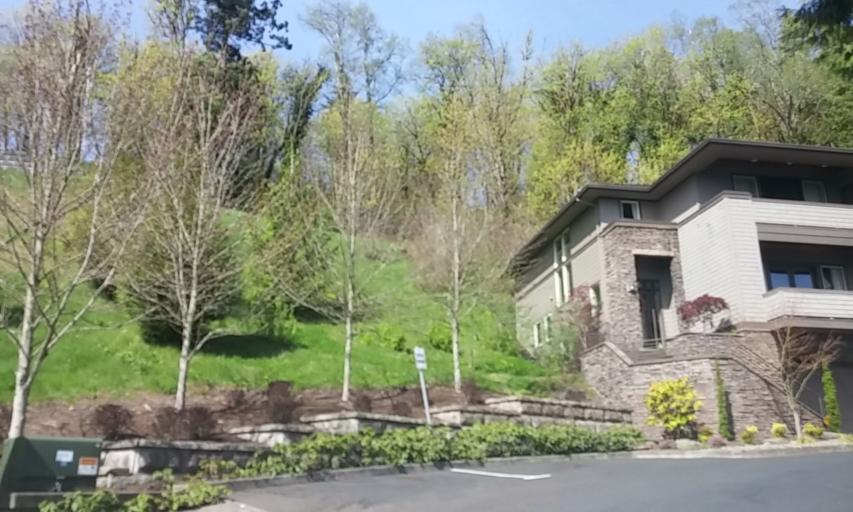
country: US
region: Oregon
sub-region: Washington County
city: West Haven-Sylvan
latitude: 45.5238
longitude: -122.7453
